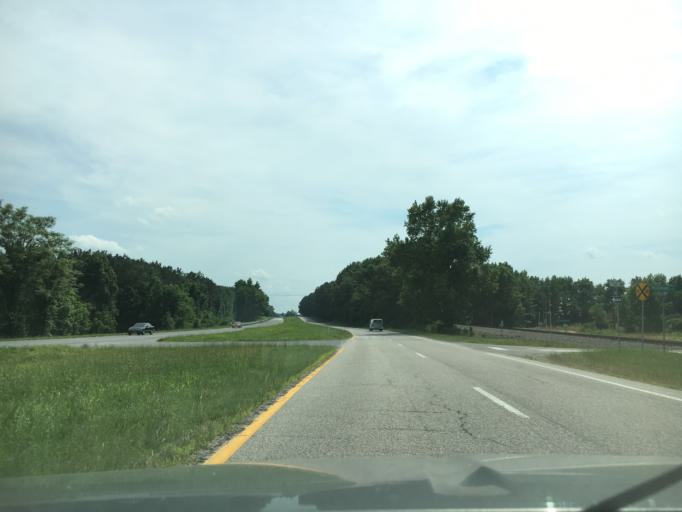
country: US
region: Virginia
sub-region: Nottoway County
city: Crewe
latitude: 37.2067
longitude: -78.1644
